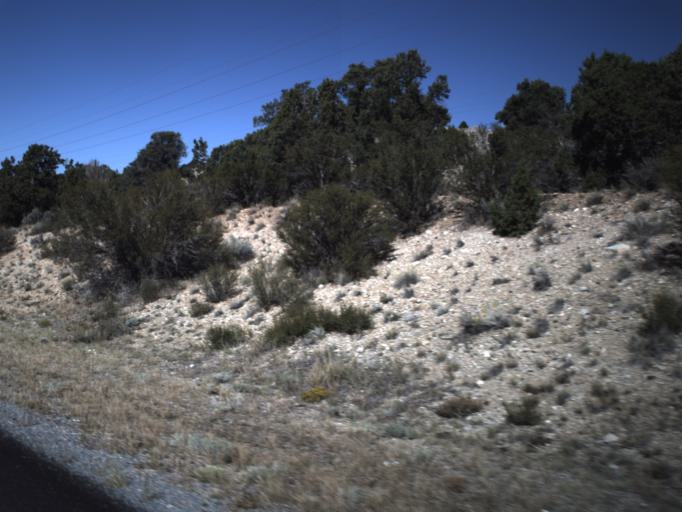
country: US
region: Utah
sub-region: Iron County
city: Cedar City
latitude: 37.6112
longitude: -113.3881
